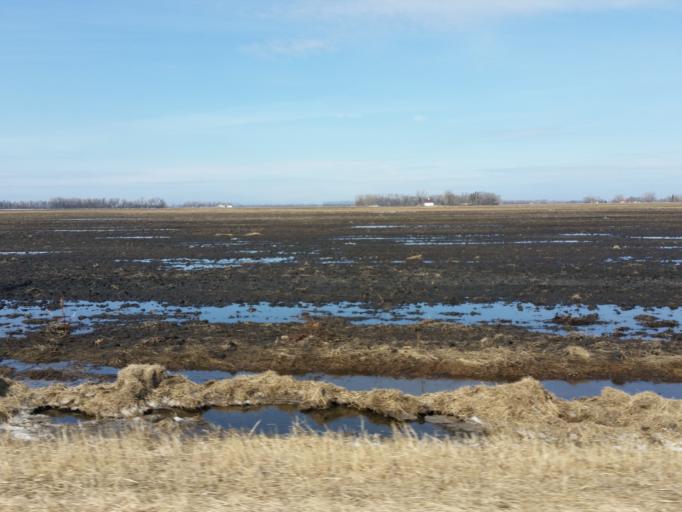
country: US
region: North Dakota
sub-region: Walsh County
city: Grafton
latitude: 48.4413
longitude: -97.4107
